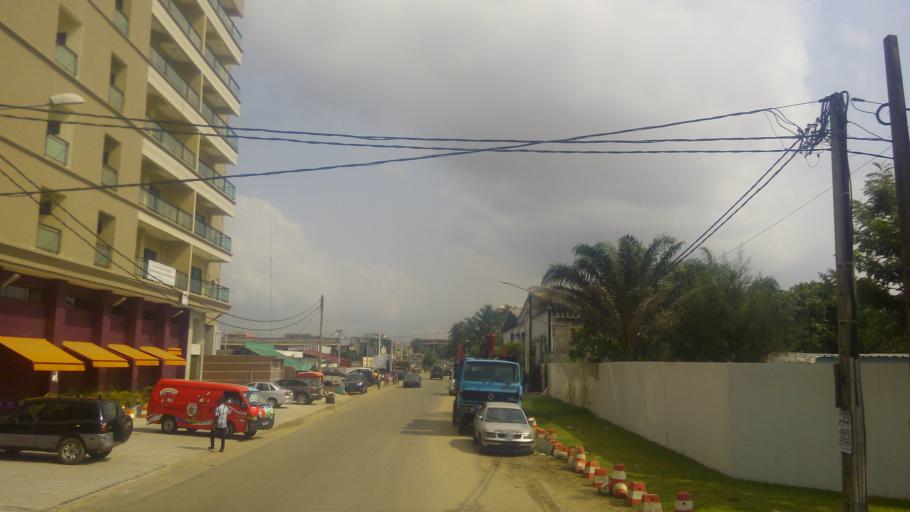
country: CI
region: Lagunes
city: Abidjan
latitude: 5.2737
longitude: -3.9776
